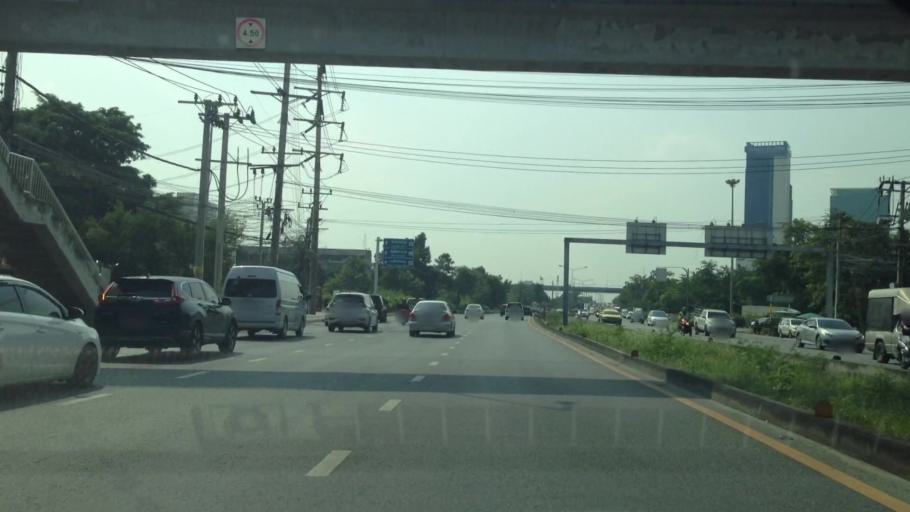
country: TH
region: Bangkok
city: Bang Na
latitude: 13.6728
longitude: 100.6457
